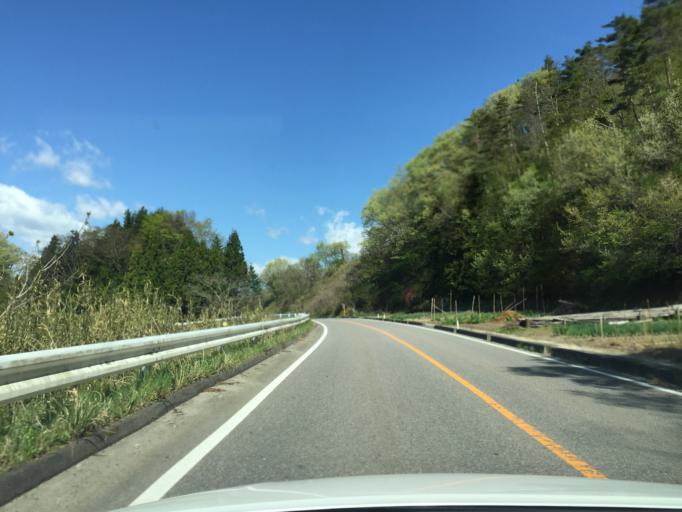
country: JP
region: Fukushima
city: Nihommatsu
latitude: 37.5540
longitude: 140.5224
